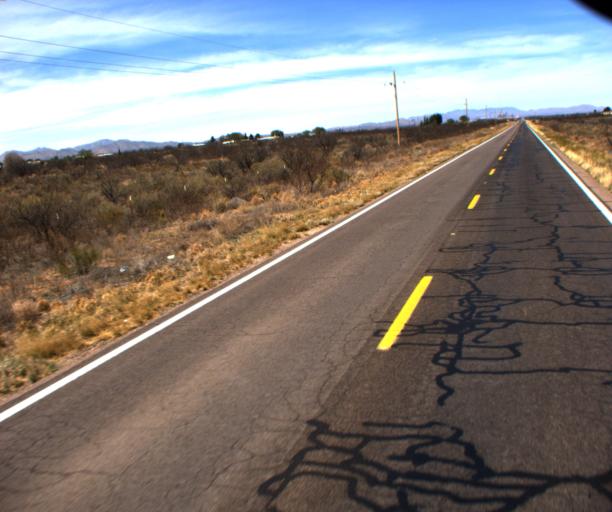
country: US
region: Arizona
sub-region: Cochise County
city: Willcox
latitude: 32.0008
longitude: -109.8613
